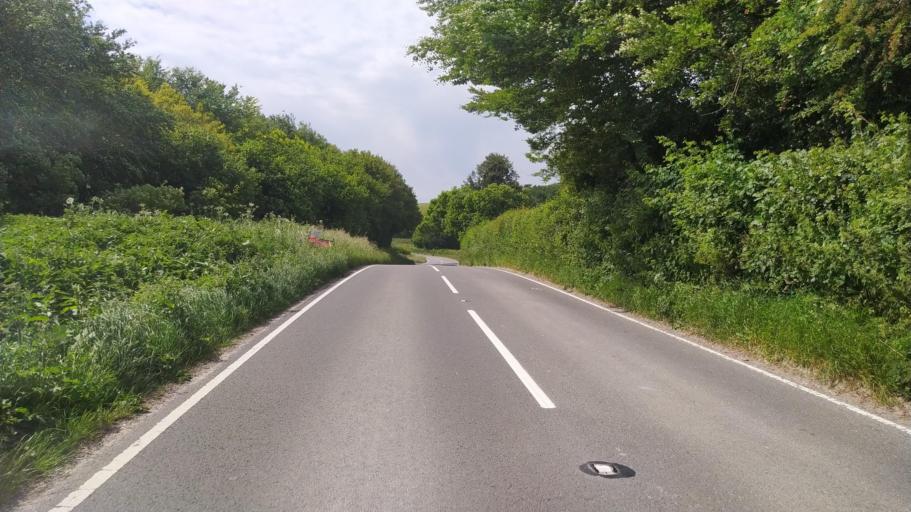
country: GB
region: England
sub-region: Dorset
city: Dorchester
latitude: 50.7985
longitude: -2.4789
